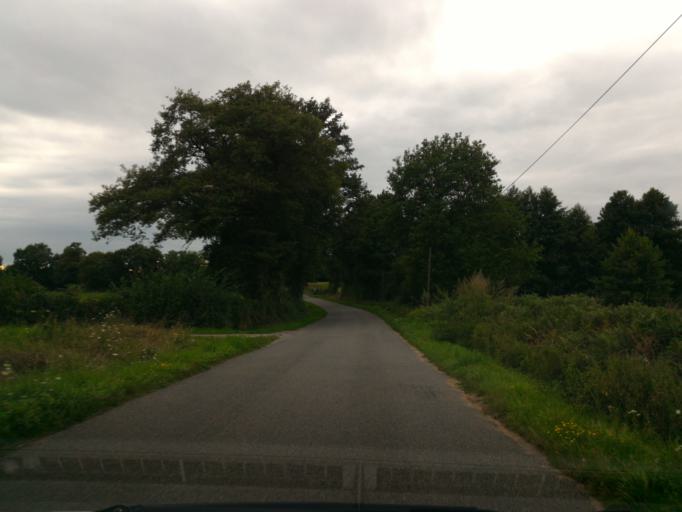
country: FR
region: Poitou-Charentes
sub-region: Departement de la Charente
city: Etagnac
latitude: 45.9469
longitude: 0.7915
